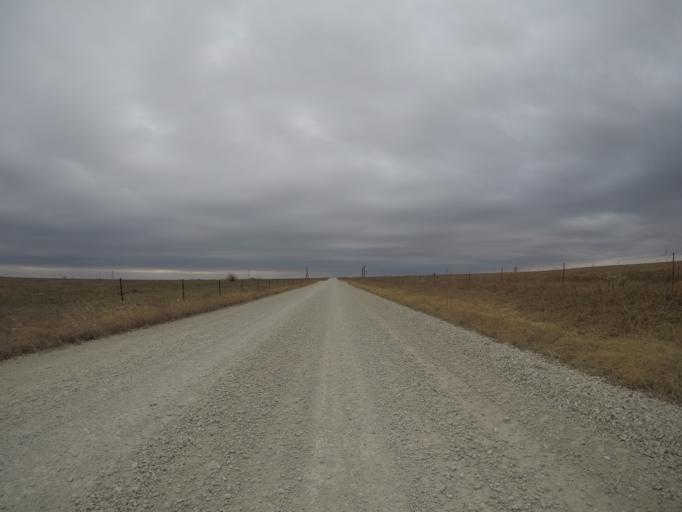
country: US
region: Kansas
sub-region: Wabaunsee County
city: Alma
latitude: 38.7598
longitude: -96.1497
